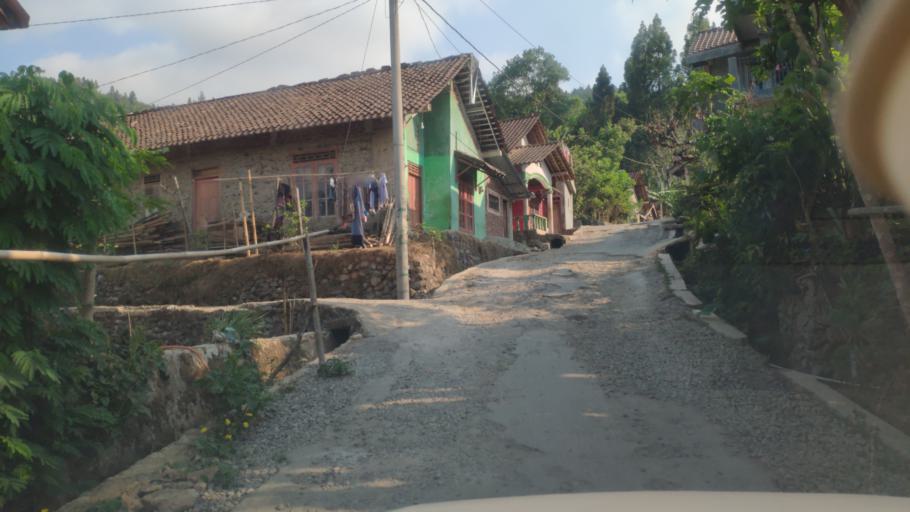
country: ID
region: Central Java
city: Wonosobo
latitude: -7.4235
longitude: 109.7399
